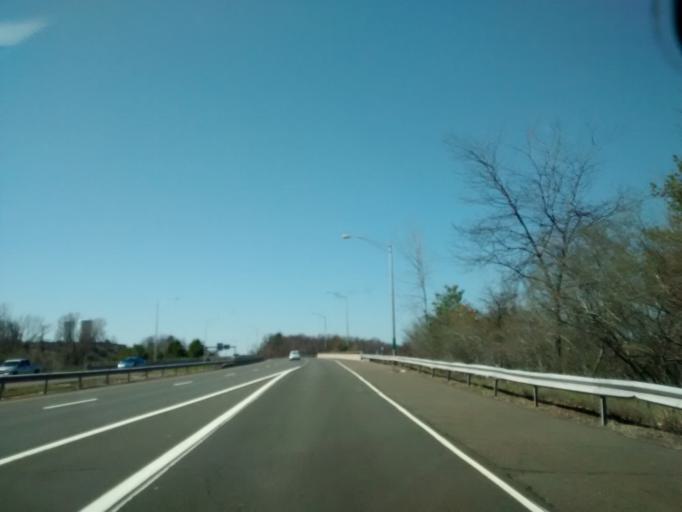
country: US
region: Connecticut
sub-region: Hartford County
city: East Hartford
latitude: 41.7921
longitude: -72.5700
